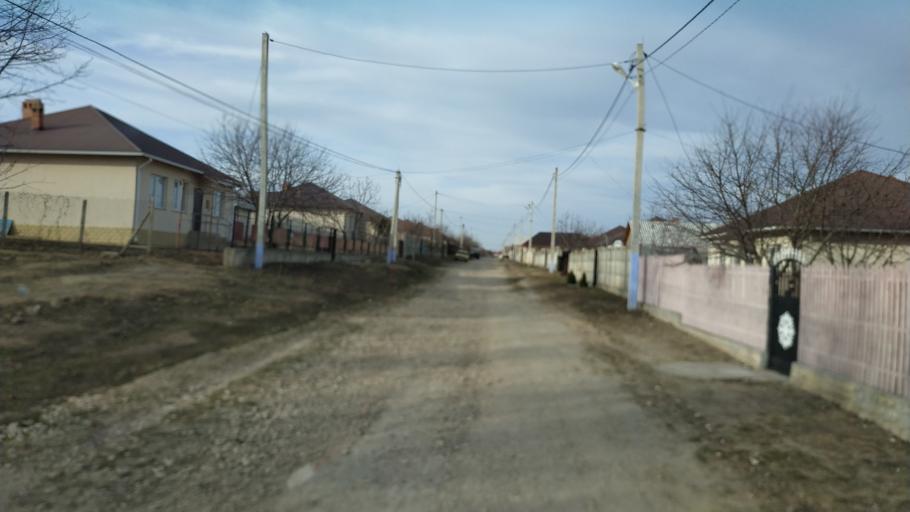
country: RO
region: Vaslui
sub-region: Comuna Dranceni
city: Dranceni
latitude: 46.8406
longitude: 28.1860
